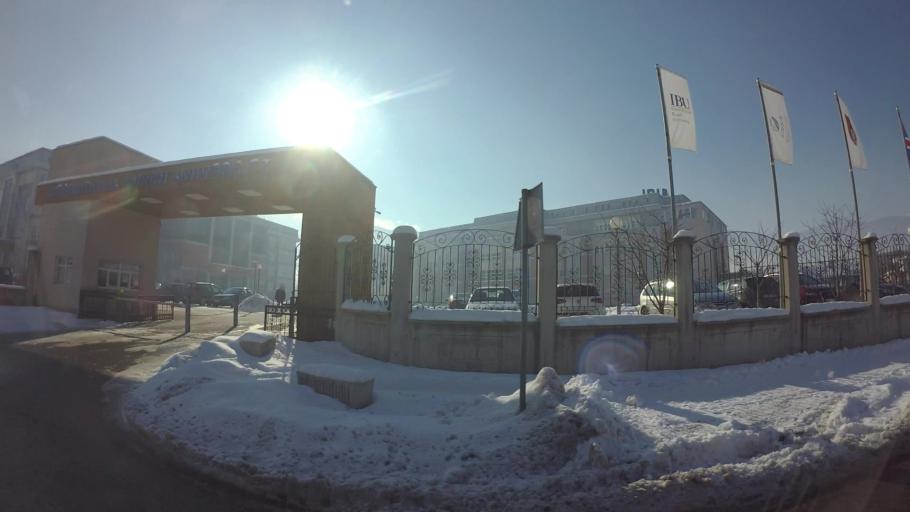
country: BA
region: Federation of Bosnia and Herzegovina
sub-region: Kanton Sarajevo
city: Sarajevo
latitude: 43.8195
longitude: 18.3119
